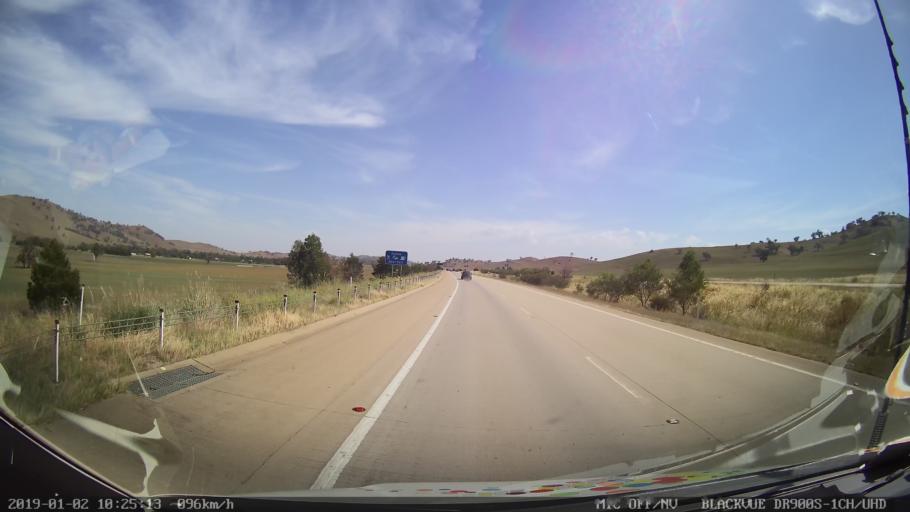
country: AU
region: New South Wales
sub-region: Gundagai
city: Gundagai
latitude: -34.9389
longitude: 148.1755
